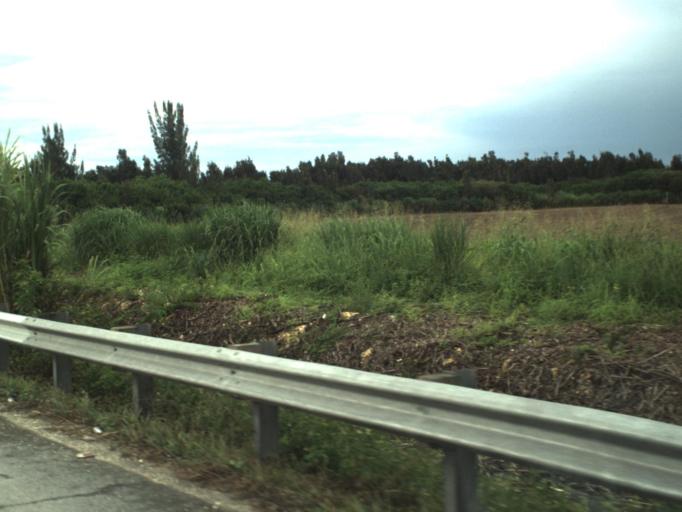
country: US
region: Florida
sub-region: Miami-Dade County
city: Kendall West
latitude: 25.7023
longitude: -80.4790
